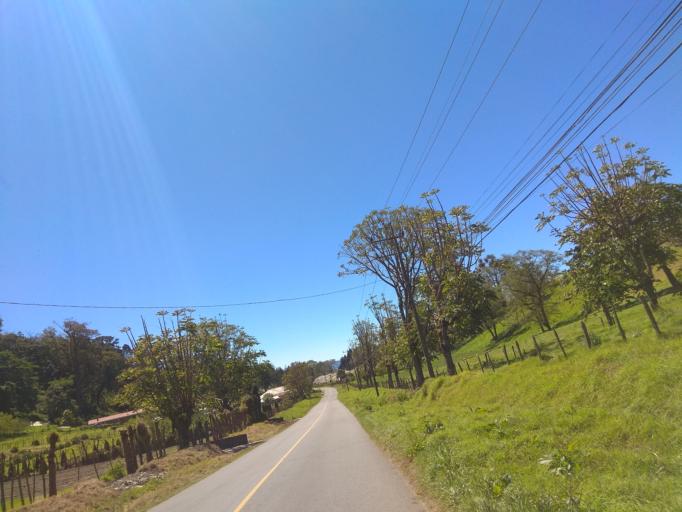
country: CR
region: Cartago
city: Tres Rios
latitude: 9.9485
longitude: -83.9314
